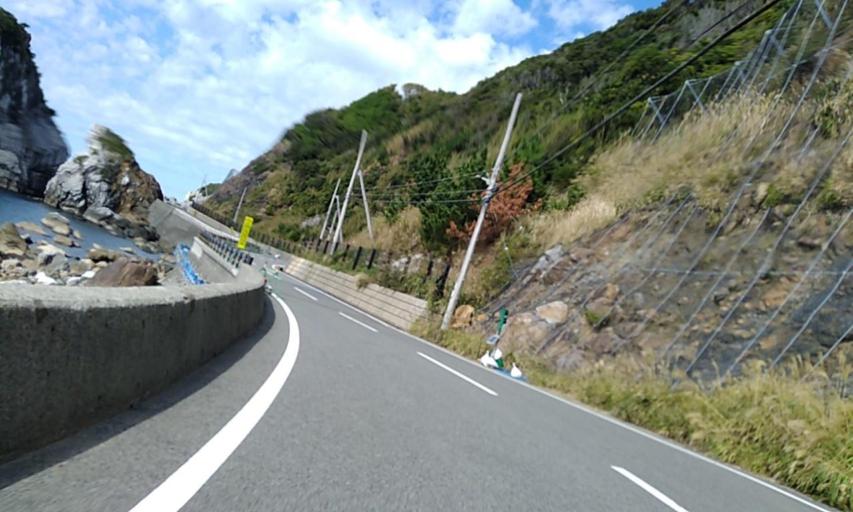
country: JP
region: Wakayama
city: Gobo
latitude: 33.9732
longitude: 135.0786
